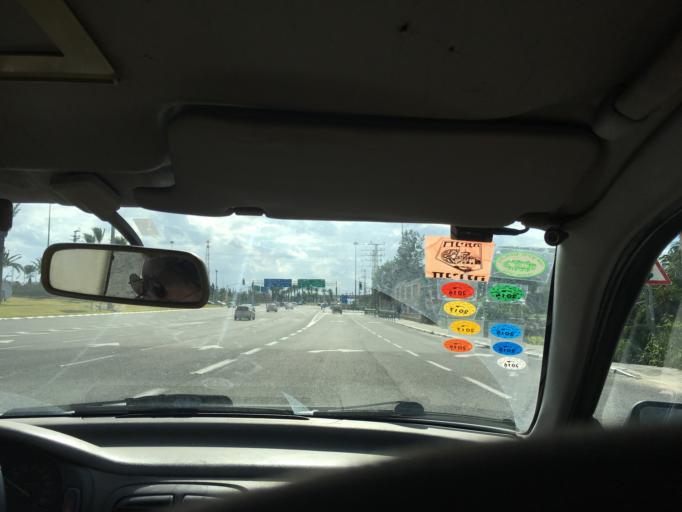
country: IL
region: Tel Aviv
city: Ramat HaSharon
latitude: 32.1368
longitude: 34.8343
